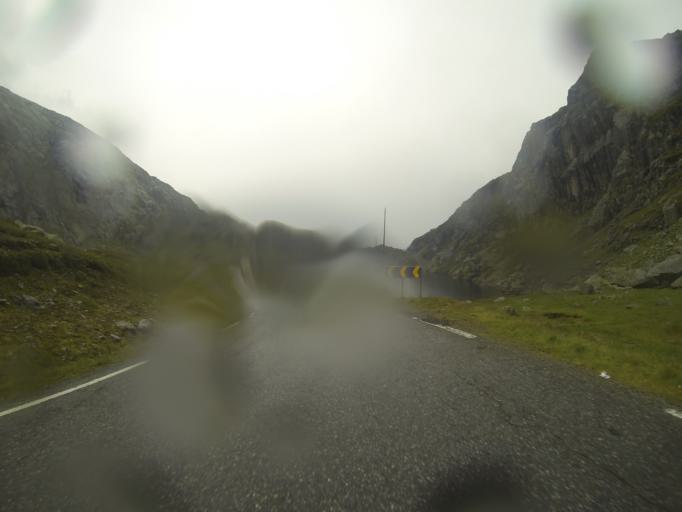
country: NO
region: Hordaland
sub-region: Odda
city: Odda
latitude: 59.7711
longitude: 6.7426
